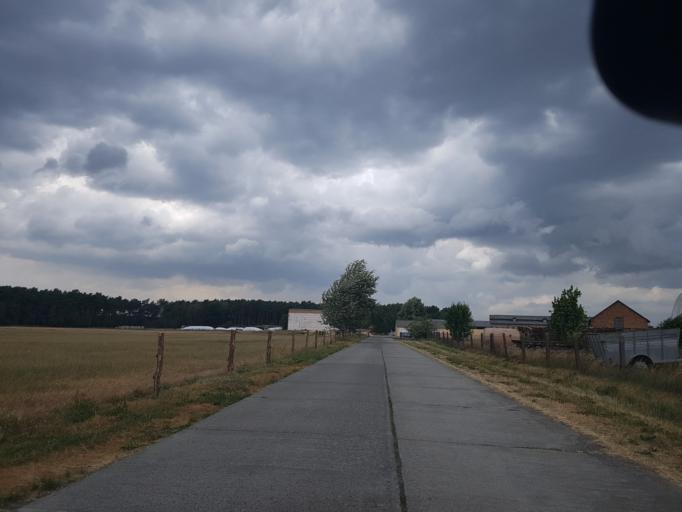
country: DE
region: Brandenburg
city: Treuenbrietzen
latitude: 52.0370
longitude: 12.8046
